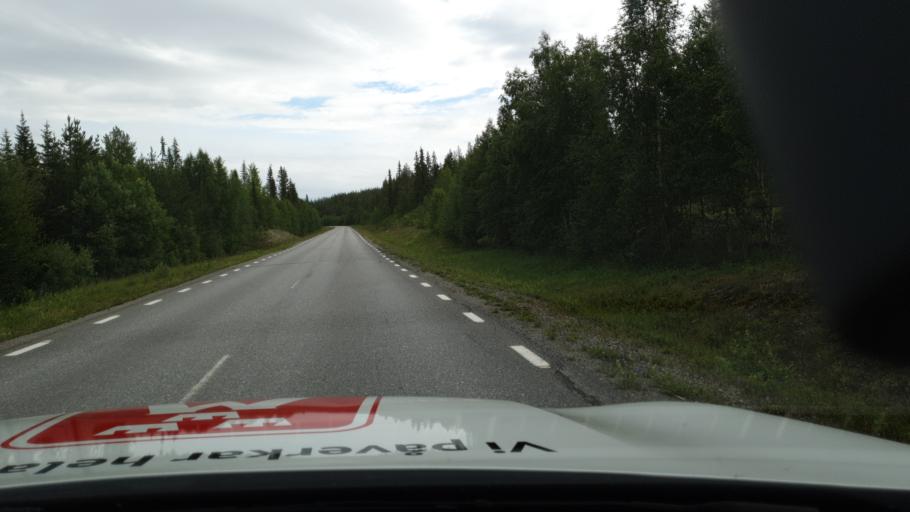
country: SE
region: Vaesterbotten
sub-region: Sorsele Kommun
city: Sorsele
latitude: 65.5145
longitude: 17.3269
